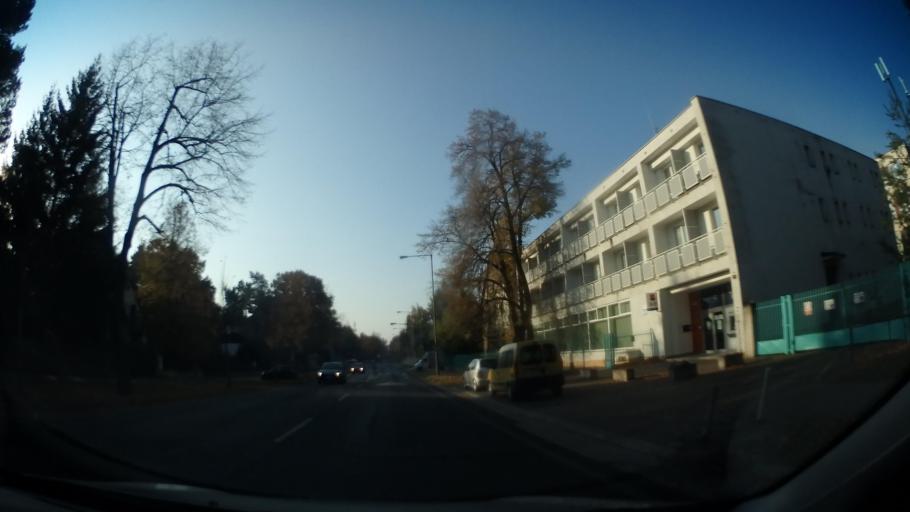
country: CZ
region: Central Bohemia
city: Sestajovice
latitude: 50.0908
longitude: 14.6669
